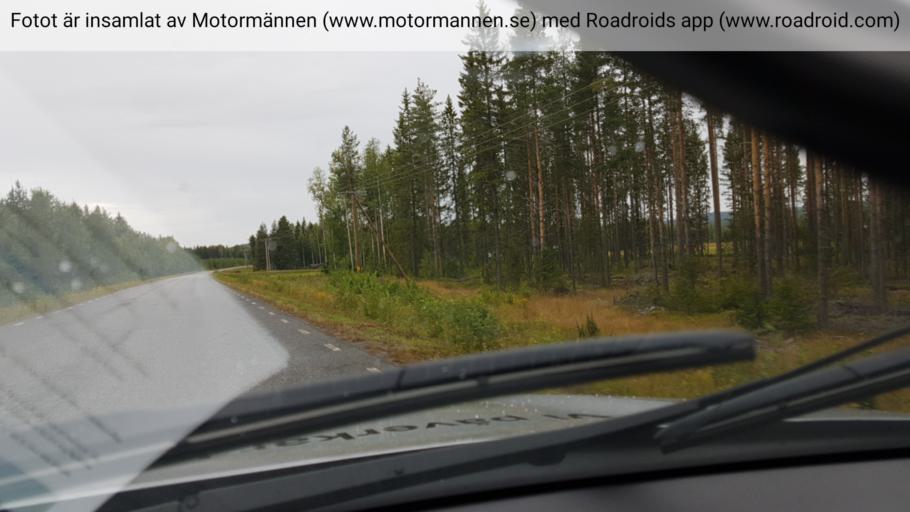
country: SE
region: Norrbotten
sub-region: Bodens Kommun
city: Boden
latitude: 65.8372
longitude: 21.4901
